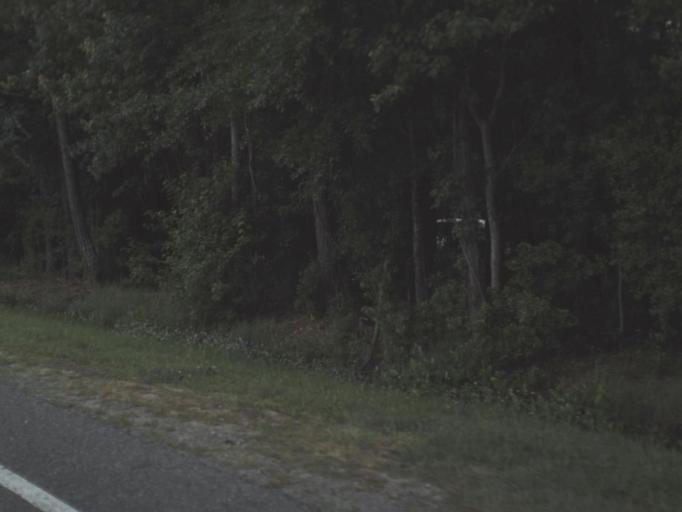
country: US
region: Florida
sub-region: Saint Johns County
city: Saint Augustine Shores
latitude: 29.7590
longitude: -81.3134
